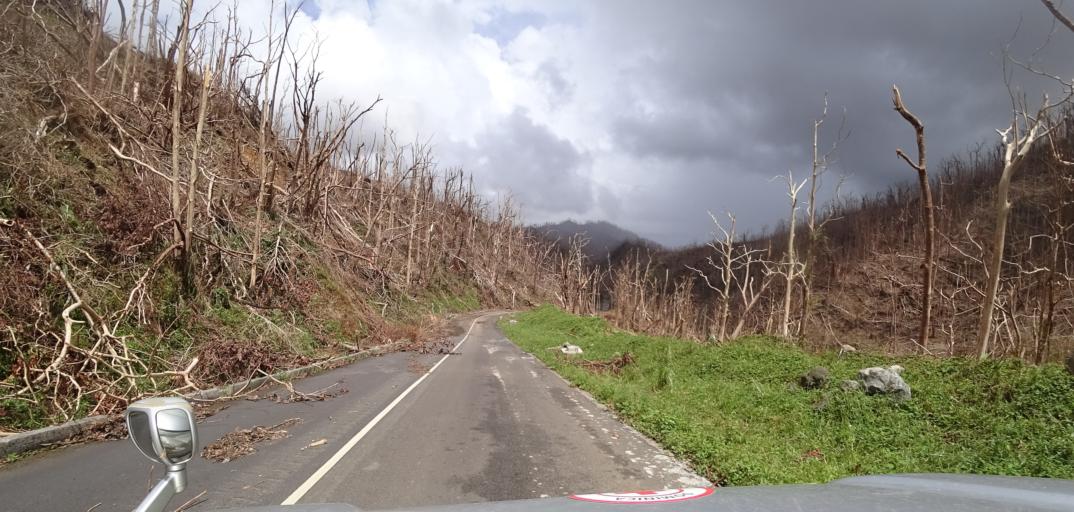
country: DM
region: Saint David
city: Castle Bruce
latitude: 15.4657
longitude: -61.3044
